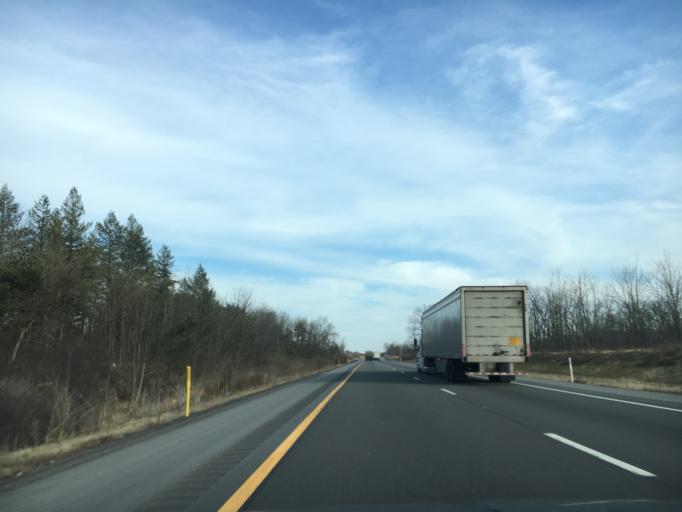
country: US
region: Pennsylvania
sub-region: Montour County
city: Danville
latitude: 40.9990
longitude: -76.6319
